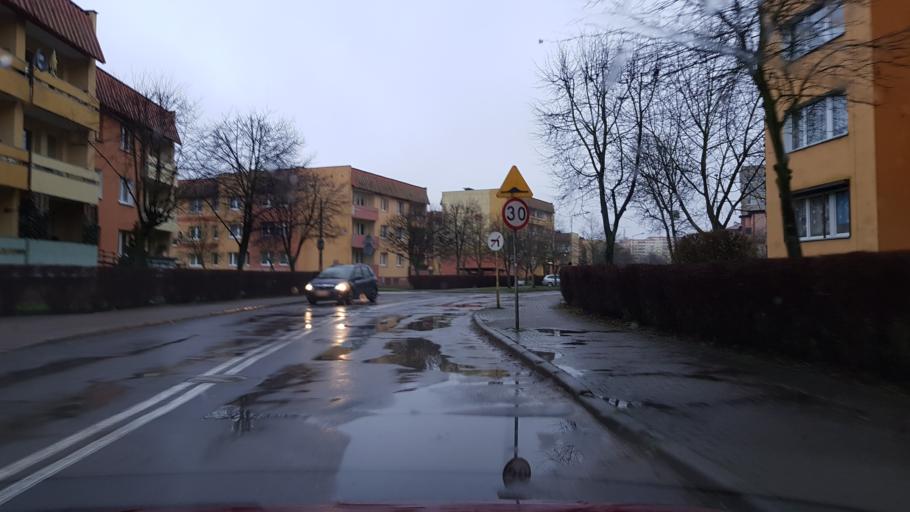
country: PL
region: West Pomeranian Voivodeship
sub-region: Powiat policki
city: Police
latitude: 53.5416
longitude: 14.5431
